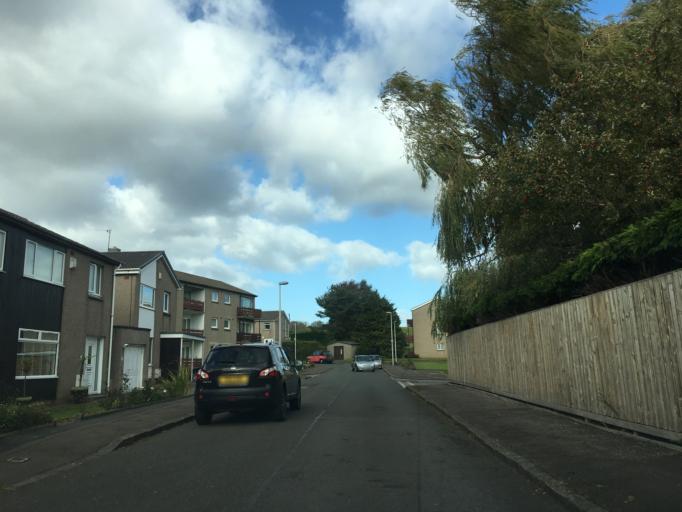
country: GB
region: Scotland
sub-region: Edinburgh
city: Currie
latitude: 55.9425
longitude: -3.3142
